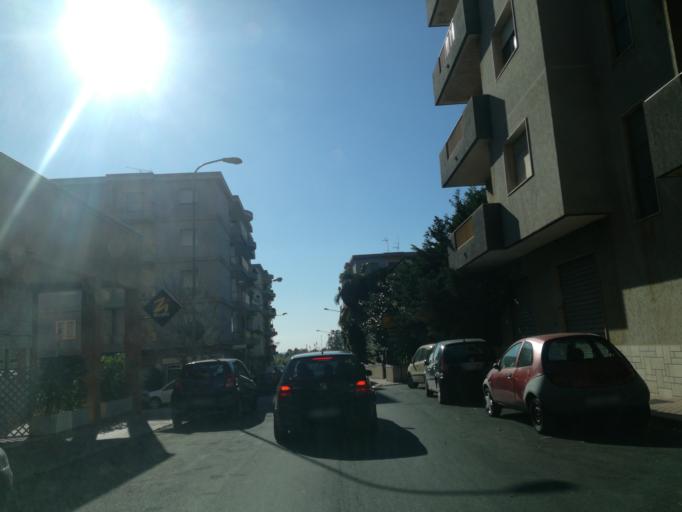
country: IT
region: Sicily
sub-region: Provincia di Caltanissetta
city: Gela
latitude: 37.0738
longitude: 14.2279
